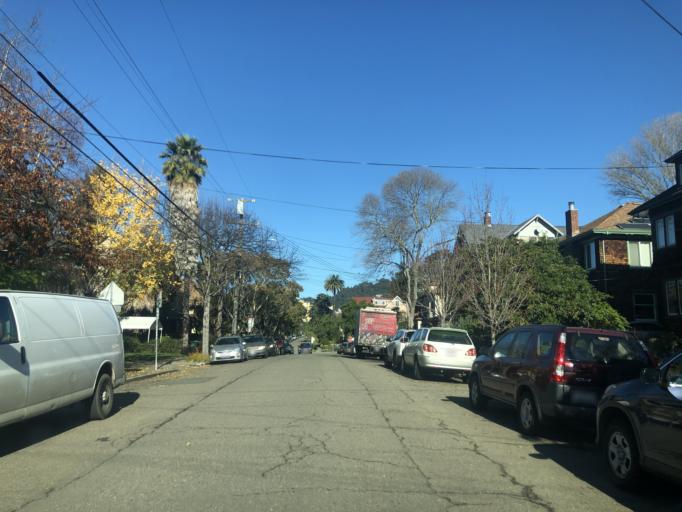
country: US
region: California
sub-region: Alameda County
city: Berkeley
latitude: 37.8606
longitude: -122.2547
